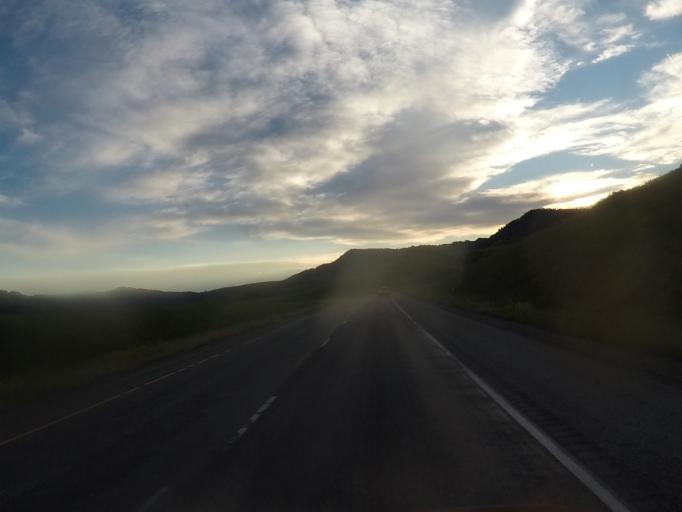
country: US
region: Montana
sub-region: Park County
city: Livingston
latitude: 45.6634
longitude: -110.7127
